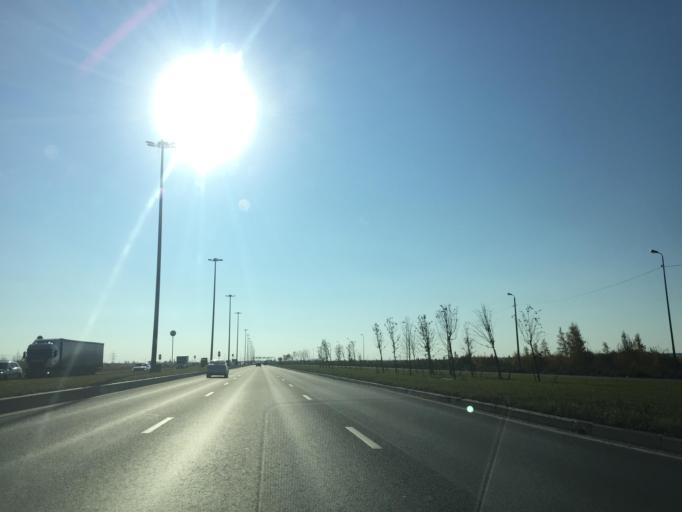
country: RU
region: St.-Petersburg
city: Petro-Slavyanka
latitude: 59.7776
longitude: 30.4981
